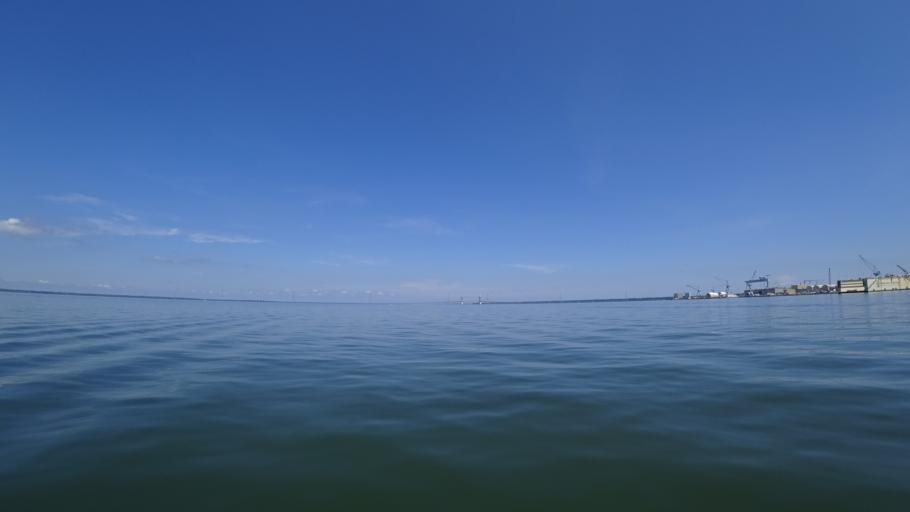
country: US
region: Virginia
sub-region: City of Newport News
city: Newport News
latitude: 36.9830
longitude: -76.4499
